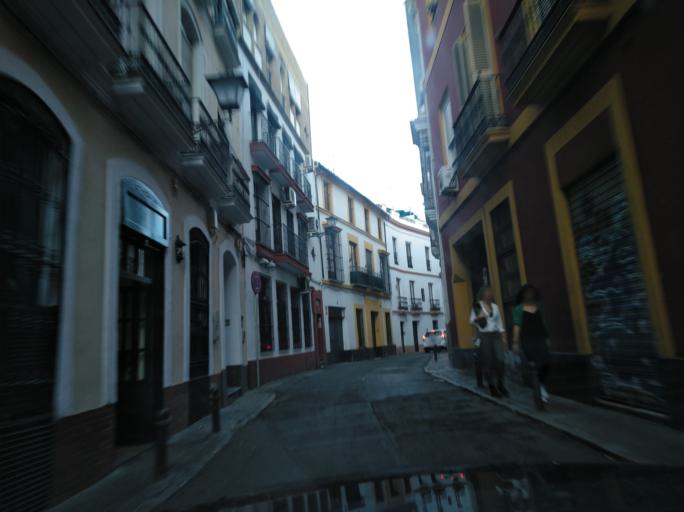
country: ES
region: Andalusia
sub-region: Provincia de Sevilla
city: Sevilla
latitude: 37.3914
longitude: -5.9896
